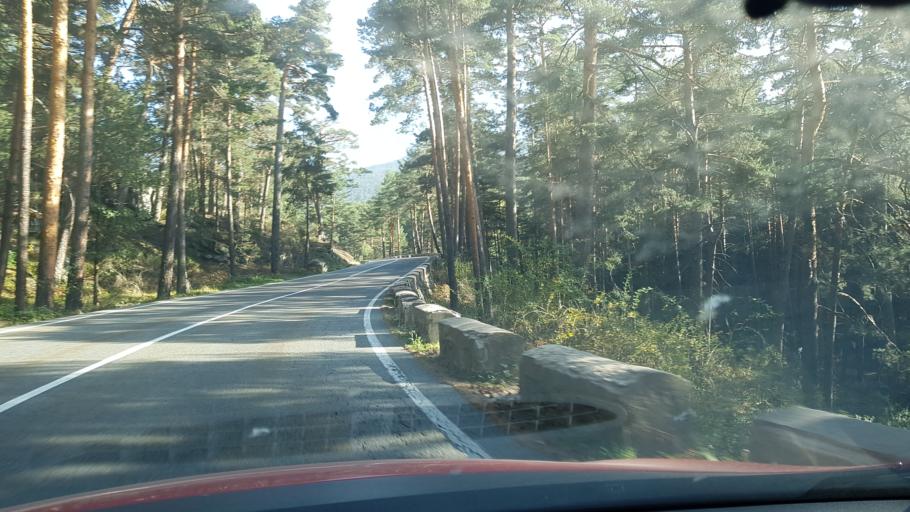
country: ES
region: Castille and Leon
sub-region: Provincia de Segovia
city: San Ildefonso
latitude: 40.8254
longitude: -4.0203
